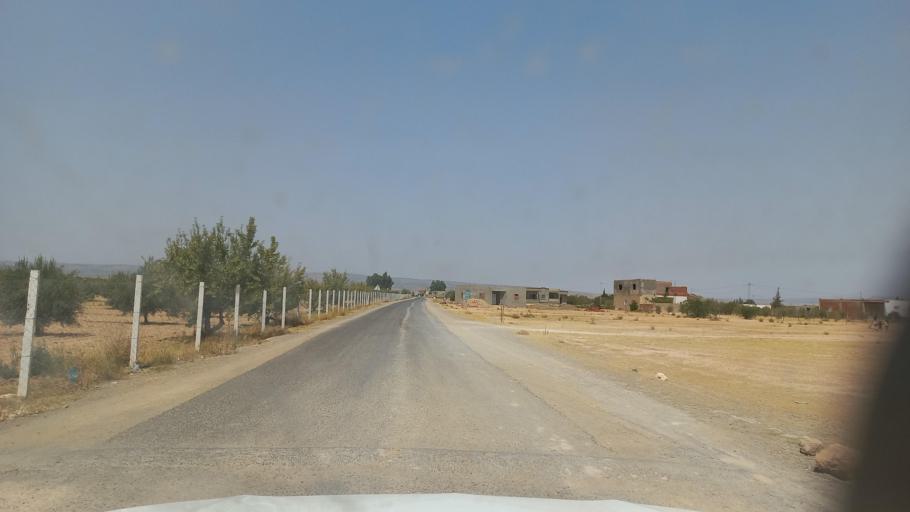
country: TN
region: Al Qasrayn
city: Kasserine
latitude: 35.2486
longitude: 9.0218
